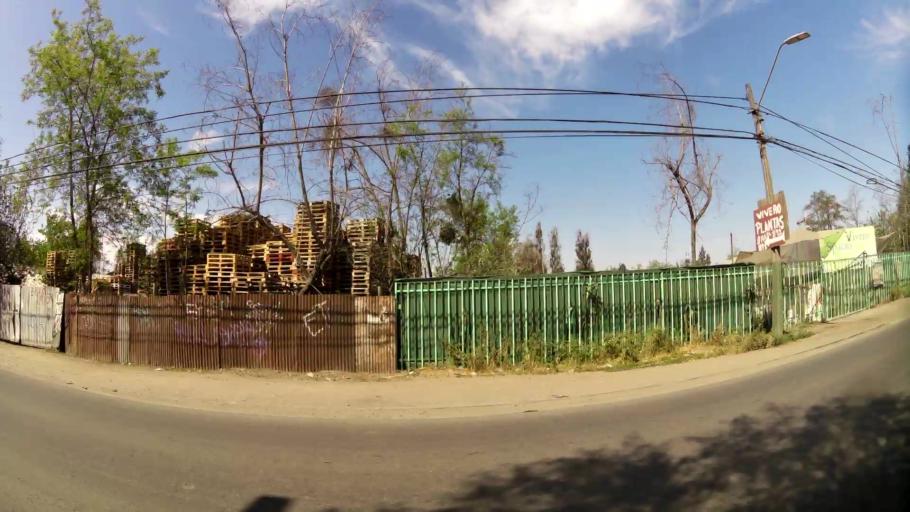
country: CL
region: Santiago Metropolitan
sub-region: Provincia de Santiago
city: Lo Prado
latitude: -33.3999
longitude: -70.7413
